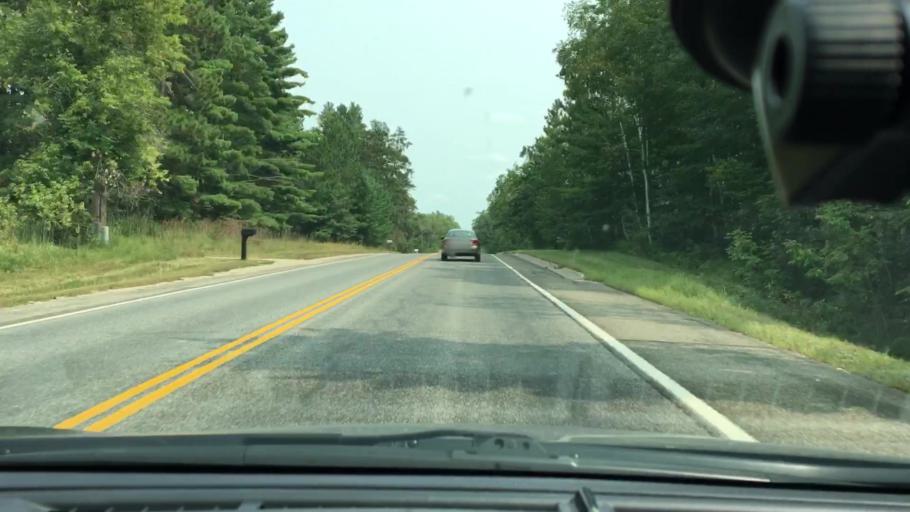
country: US
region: Minnesota
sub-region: Cass County
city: East Gull Lake
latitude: 46.4128
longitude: -94.3247
